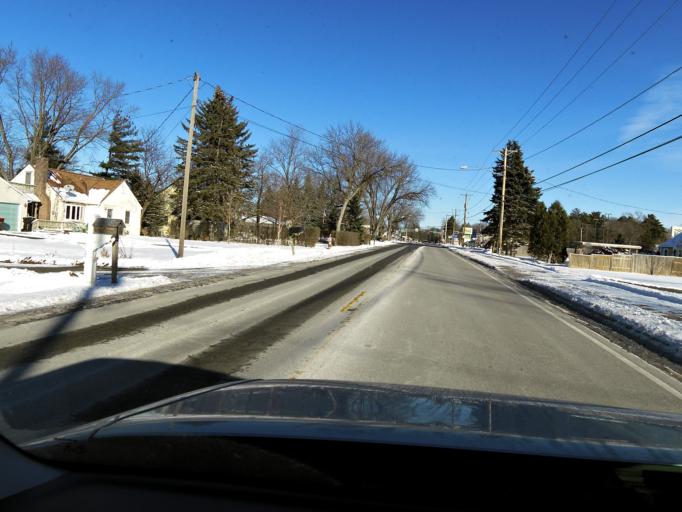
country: US
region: Minnesota
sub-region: Ramsey County
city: Maplewood
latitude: 44.9744
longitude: -92.9871
